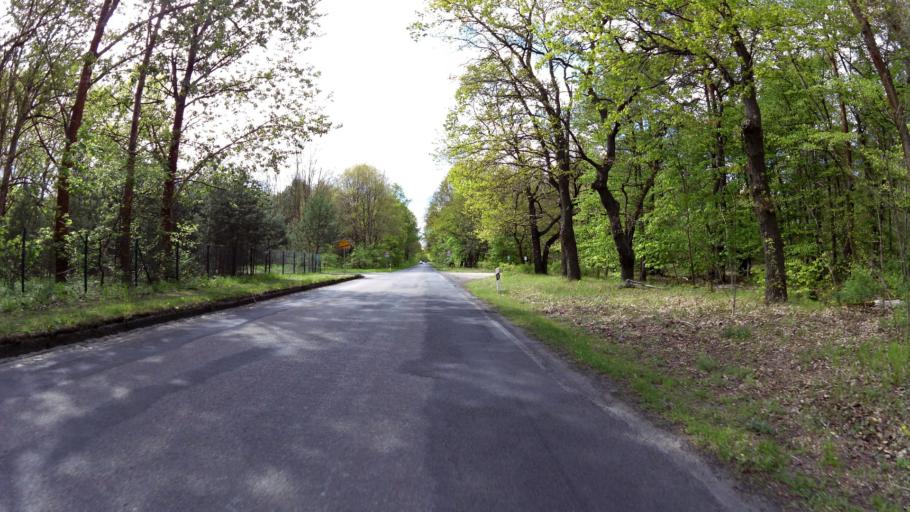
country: DE
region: Brandenburg
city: Furstenwalde
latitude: 52.3590
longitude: 14.0403
